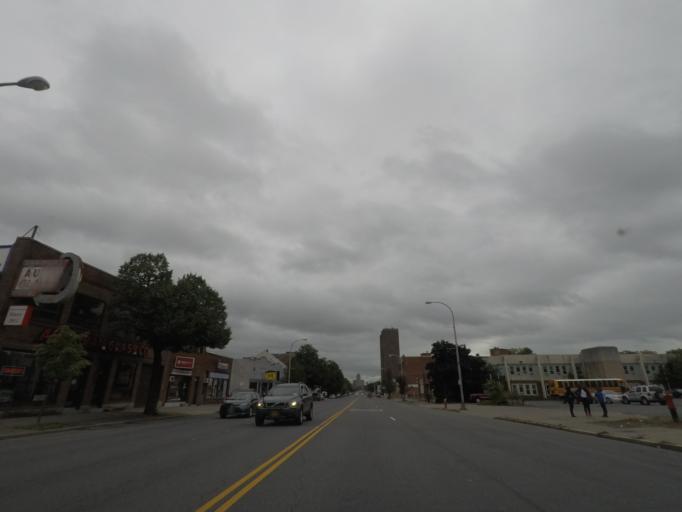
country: US
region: New York
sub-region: Albany County
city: West Albany
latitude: 42.6706
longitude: -73.7792
